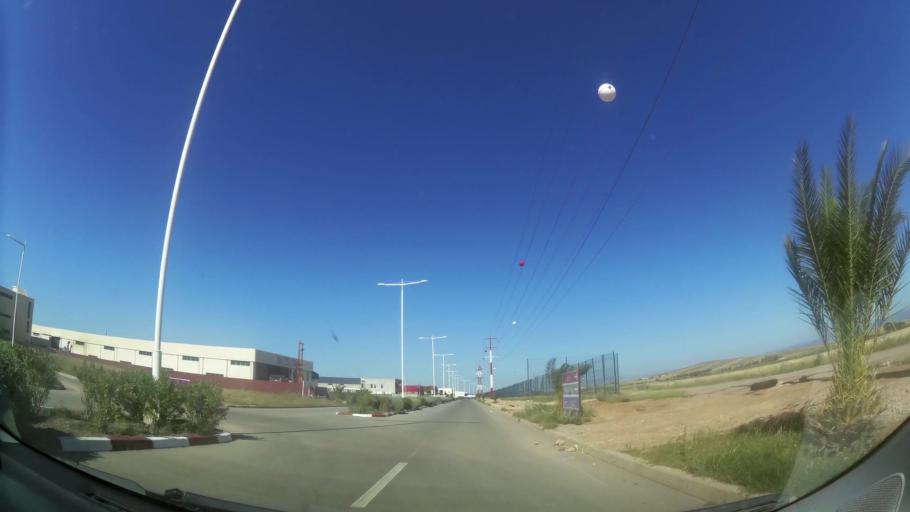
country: MA
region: Oriental
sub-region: Oujda-Angad
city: Oujda
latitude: 34.7681
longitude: -1.9360
